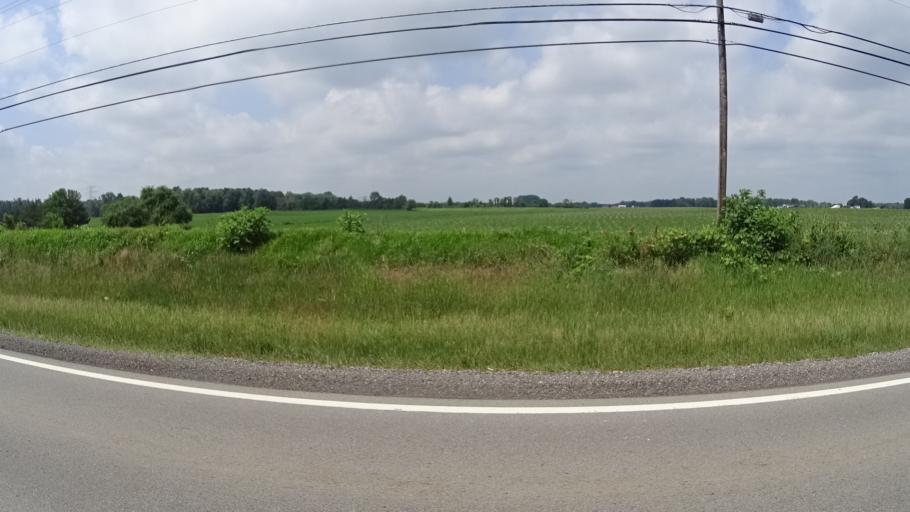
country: US
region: Ohio
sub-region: Lorain County
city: Vermilion
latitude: 41.3652
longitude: -82.3620
